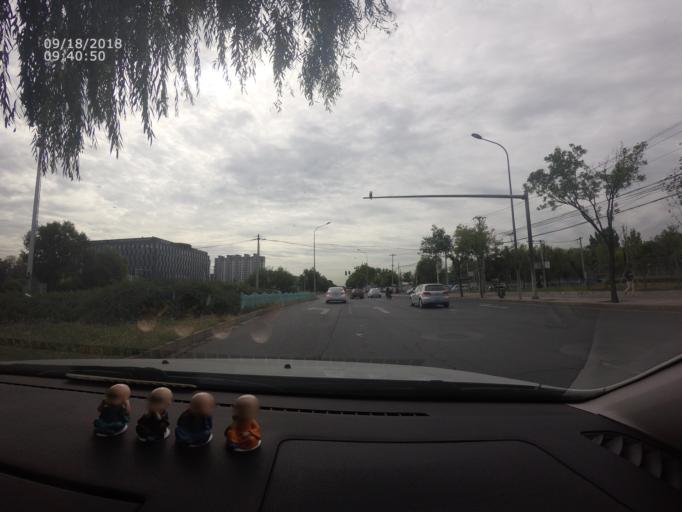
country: CN
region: Beijing
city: Xibeiwang
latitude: 40.0669
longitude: 116.2402
